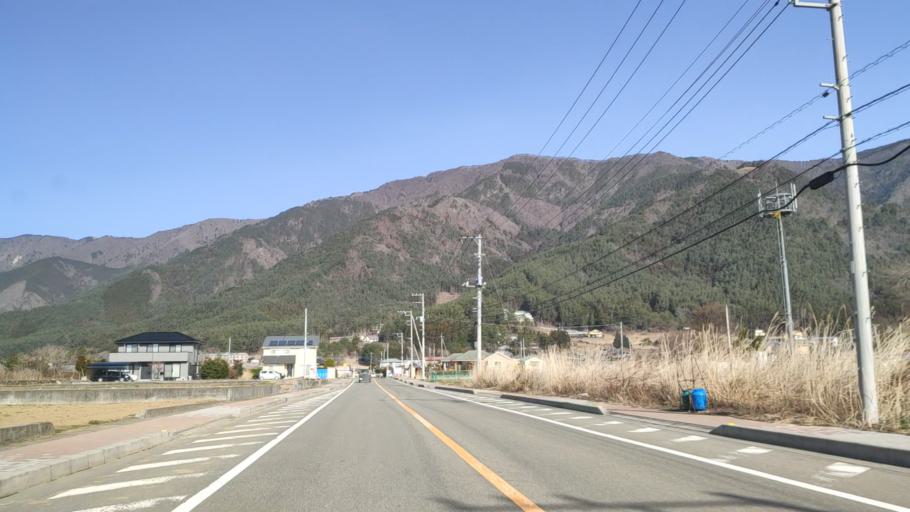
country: JP
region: Yamanashi
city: Fujikawaguchiko
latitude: 35.5220
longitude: 138.7393
